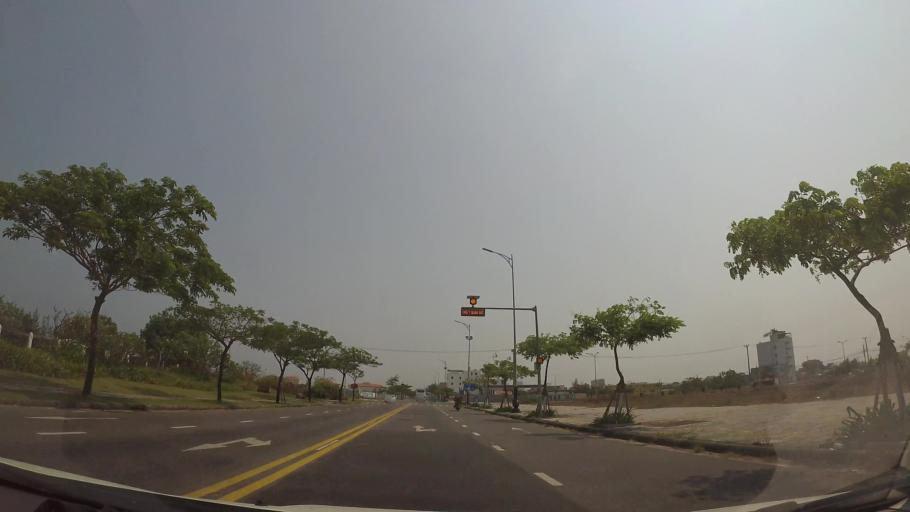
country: VN
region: Da Nang
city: Ngu Hanh Son
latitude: 15.9875
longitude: 108.2723
